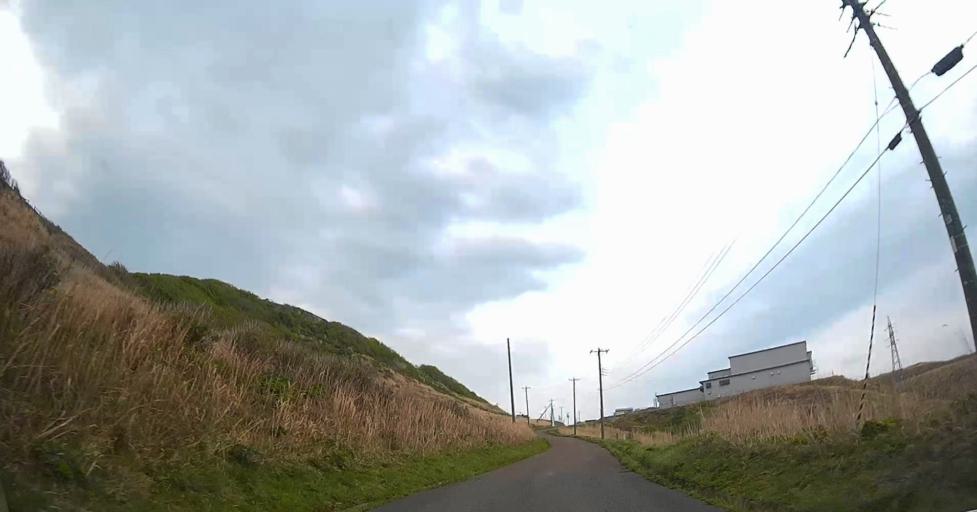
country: JP
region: Aomori
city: Shimokizukuri
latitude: 41.2539
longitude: 140.3428
